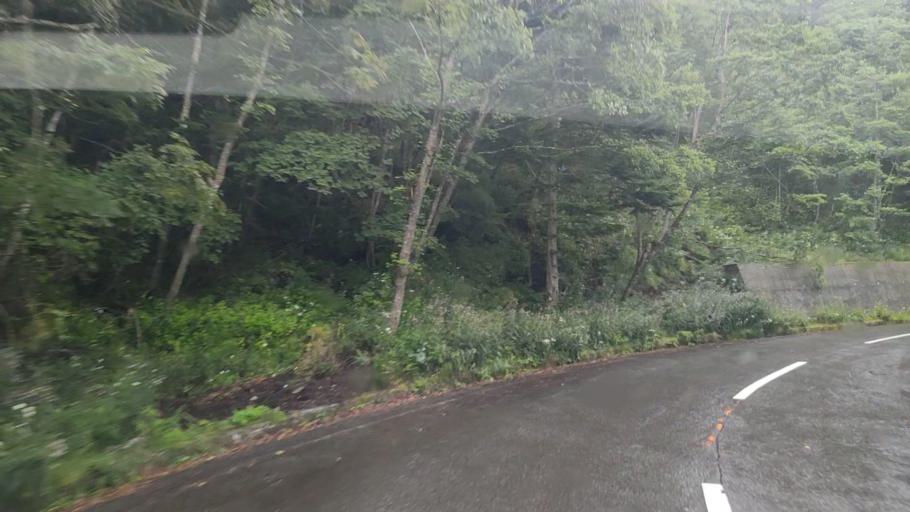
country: JP
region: Shizuoka
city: Fujinomiya
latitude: 35.3268
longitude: 138.7310
